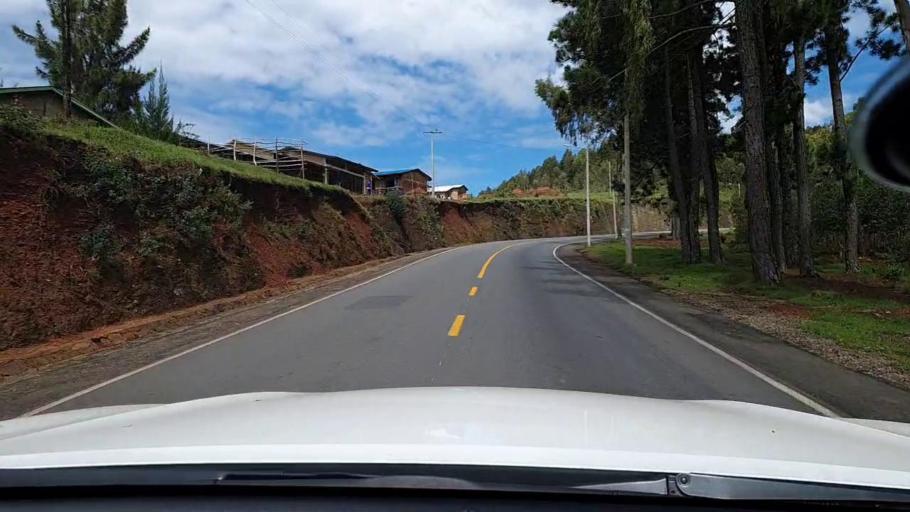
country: RW
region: Kigali
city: Kigali
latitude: -1.8277
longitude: 29.9482
